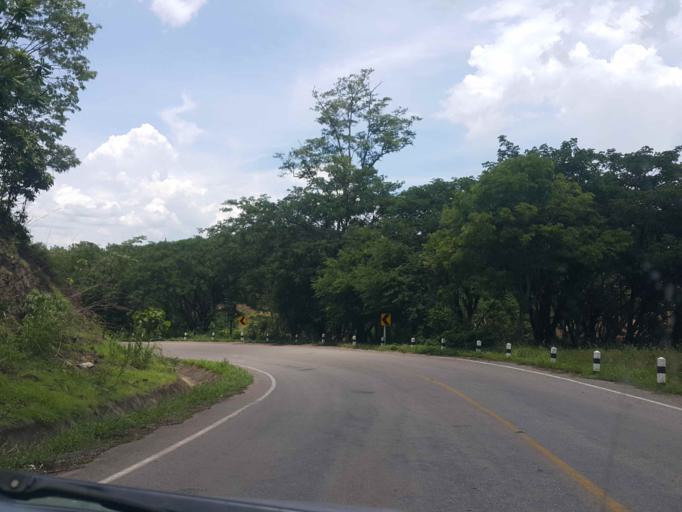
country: TH
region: Phayao
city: Chiang Muan
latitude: 18.9222
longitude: 100.2095
